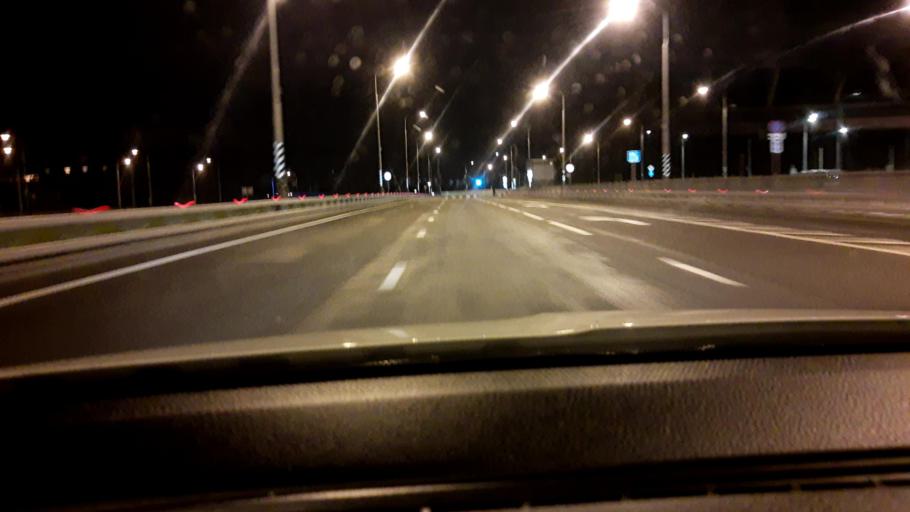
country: RU
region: Moskovskaya
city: Kommunarka
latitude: 55.5577
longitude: 37.4715
